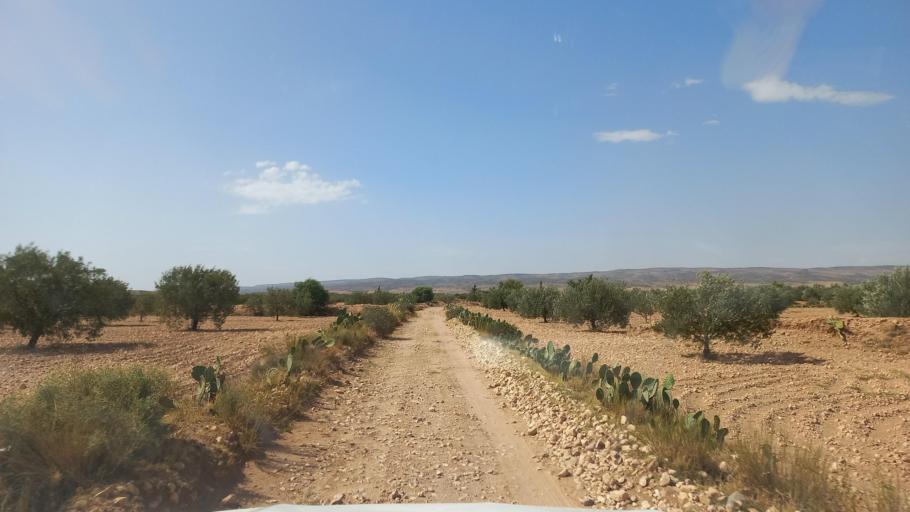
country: TN
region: Al Qasrayn
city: Kasserine
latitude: 35.2582
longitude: 8.9522
